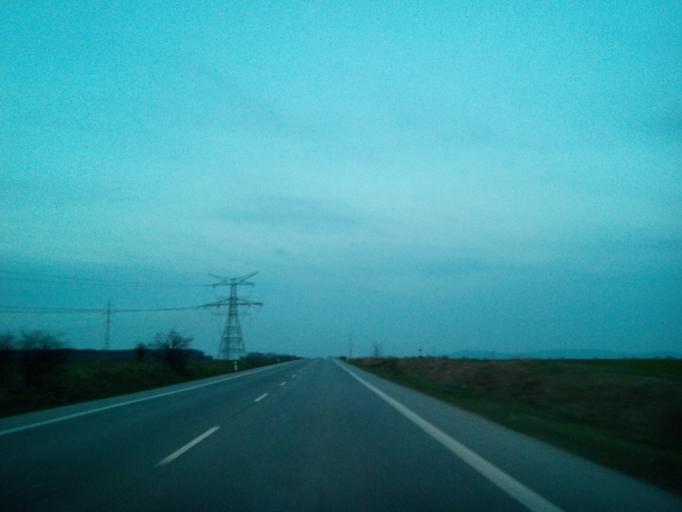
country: SK
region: Kosicky
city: Moldava nad Bodvou
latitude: 48.6032
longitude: 21.0921
